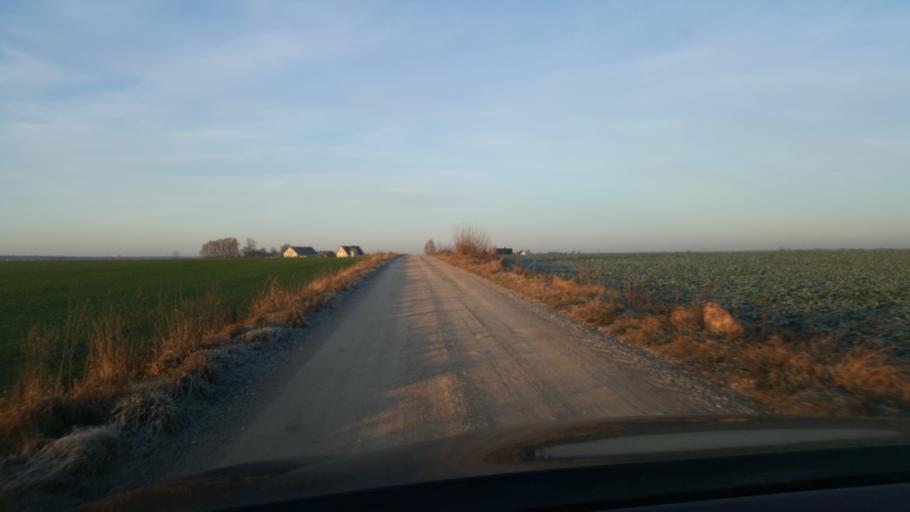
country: LT
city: Prienai
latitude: 54.4839
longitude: 23.9175
